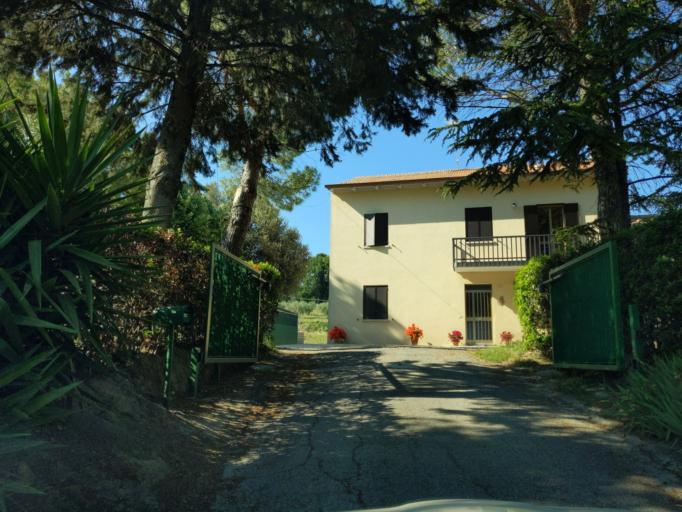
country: IT
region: The Marches
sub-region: Provincia di Pesaro e Urbino
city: Cuccurano
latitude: 43.8006
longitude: 12.9601
